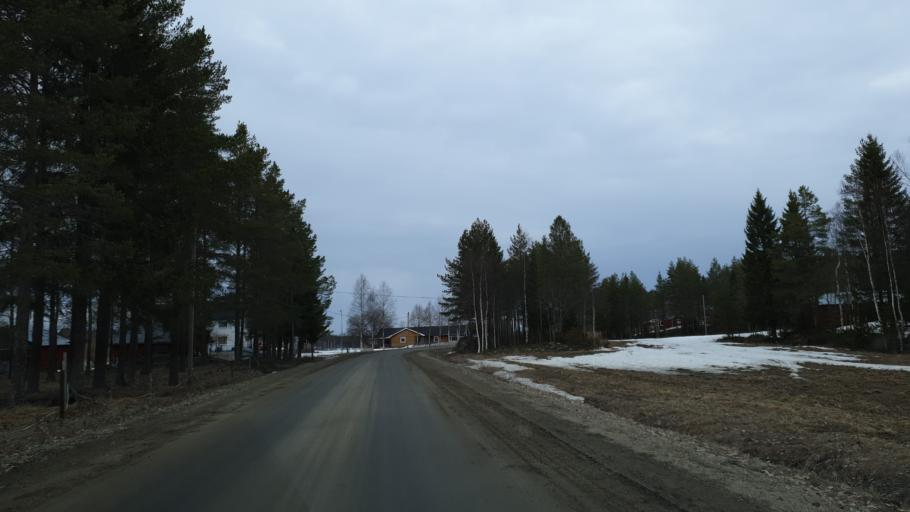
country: SE
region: Vaesterbotten
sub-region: Skelleftea Kommun
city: Burea
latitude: 64.3163
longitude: 21.1391
